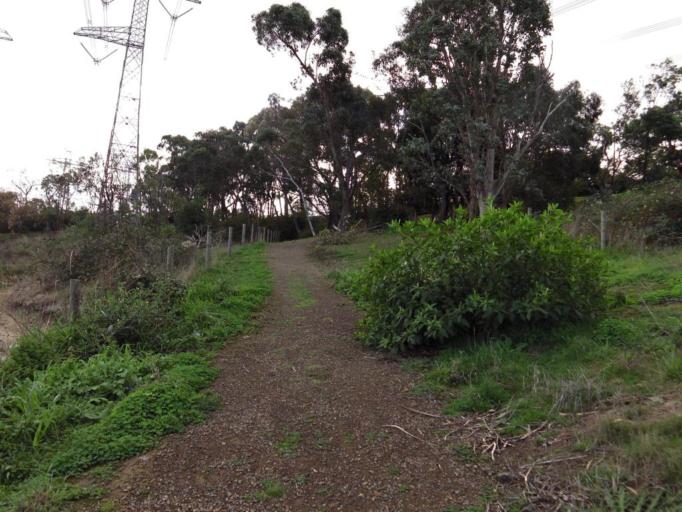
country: AU
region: Victoria
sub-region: Nillumbik
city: Eltham
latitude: -37.7503
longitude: 145.1797
